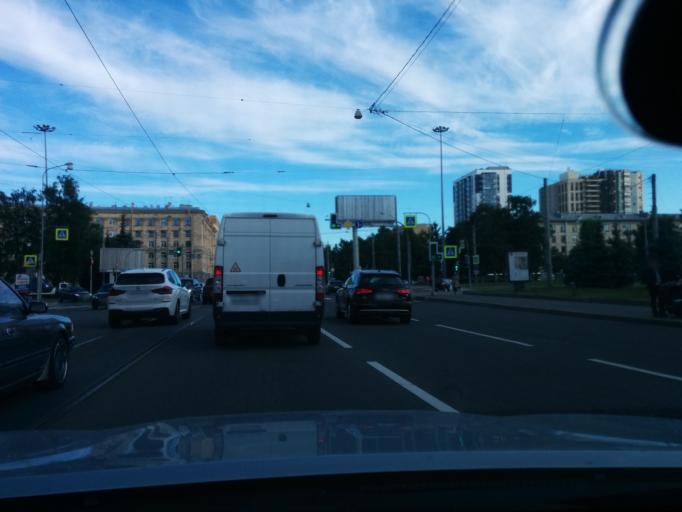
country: RU
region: Leningrad
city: Svetlanovskiy
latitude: 60.0044
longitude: 30.3272
